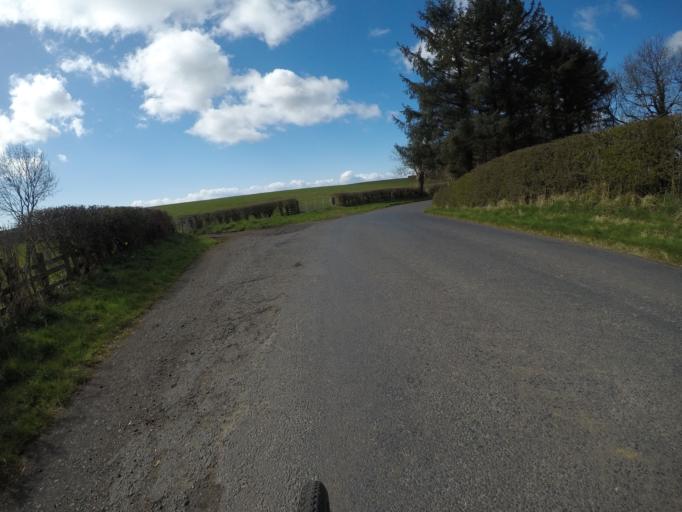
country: GB
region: Scotland
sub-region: East Ayrshire
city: Crosshouse
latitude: 55.5913
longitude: -4.5463
